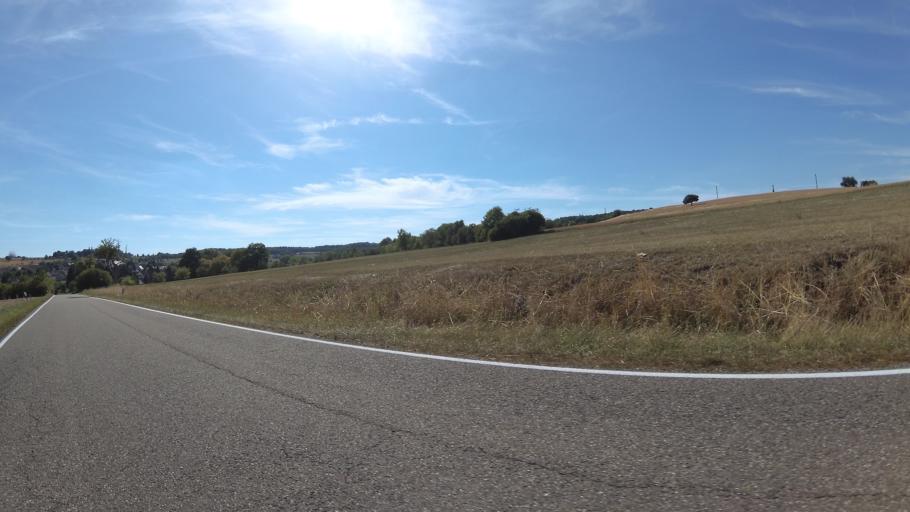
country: DE
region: Saarland
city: Gersheim
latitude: 49.1496
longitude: 7.2730
